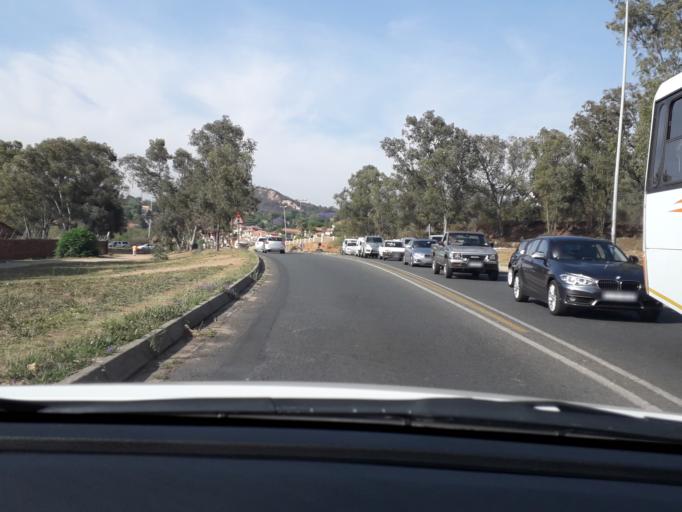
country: ZA
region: Gauteng
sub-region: City of Johannesburg Metropolitan Municipality
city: Roodepoort
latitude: -26.0766
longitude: 27.9595
